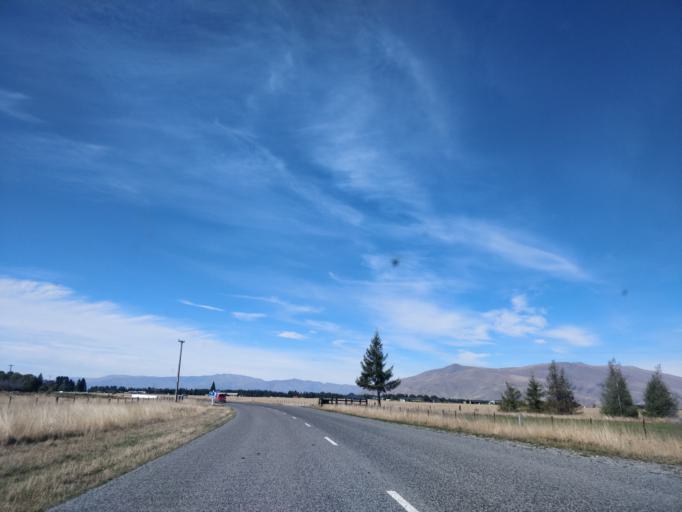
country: NZ
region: Otago
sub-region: Queenstown-Lakes District
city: Wanaka
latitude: -44.2345
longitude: 170.0706
